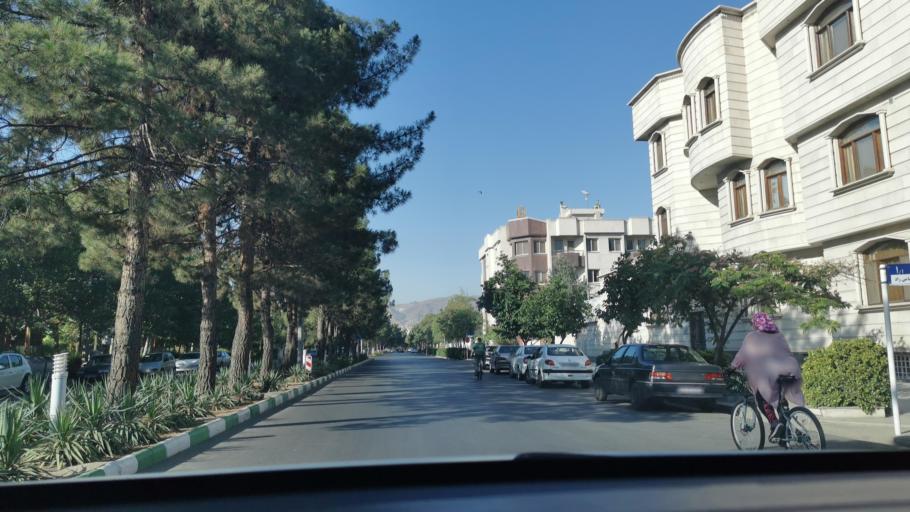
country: IR
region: Razavi Khorasan
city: Mashhad
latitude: 36.3185
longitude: 59.5273
